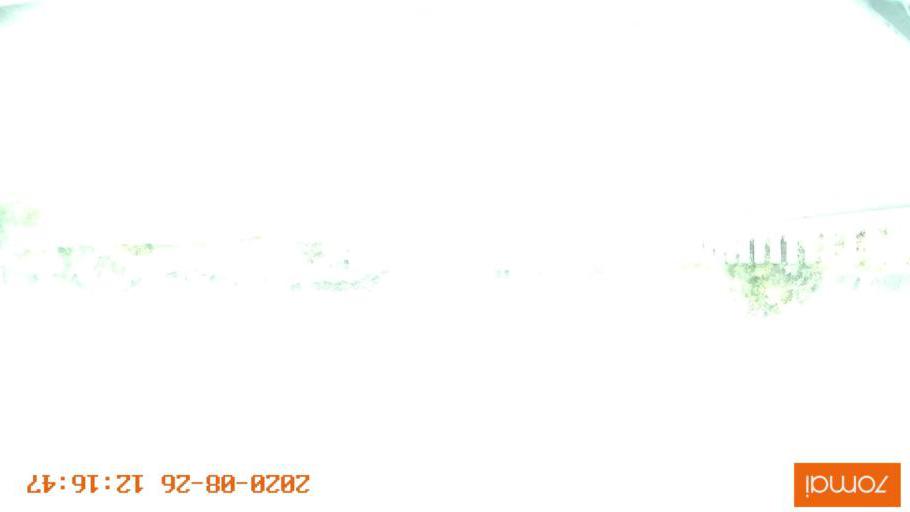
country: RU
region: Rjazan
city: Murmino
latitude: 54.4514
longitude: 40.0348
